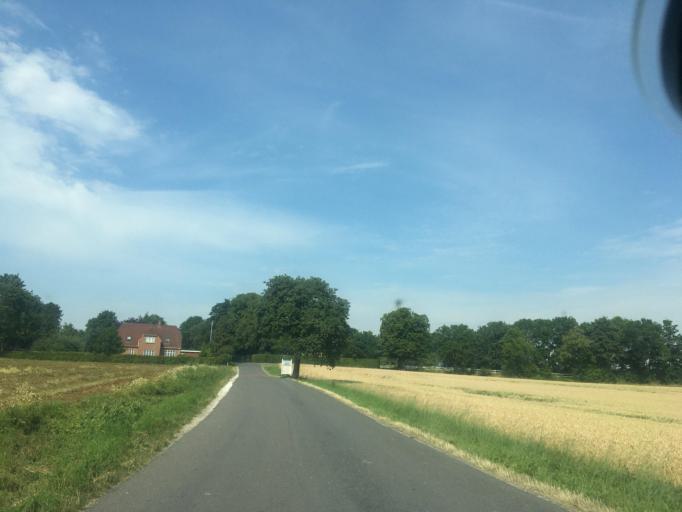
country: DK
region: Zealand
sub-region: Faxe Kommune
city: Ronnede
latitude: 55.2021
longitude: 12.0433
